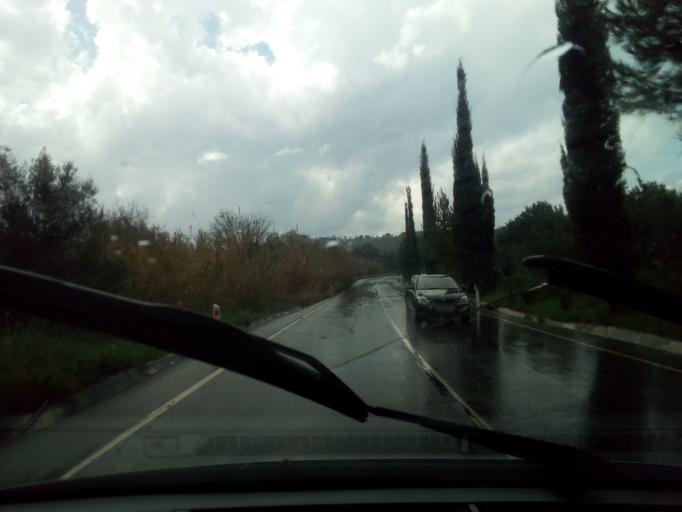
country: CY
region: Pafos
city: Polis
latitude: 35.0029
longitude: 32.4654
